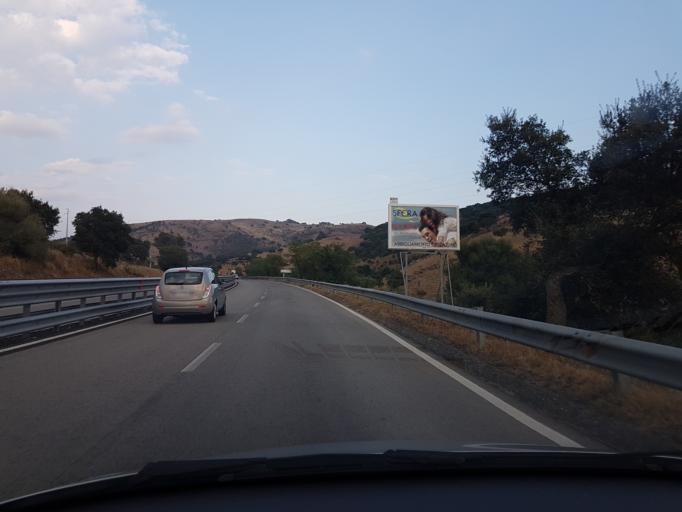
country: IT
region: Sardinia
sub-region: Provincia di Nuoro
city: Oniferi
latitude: 40.3137
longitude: 9.2341
